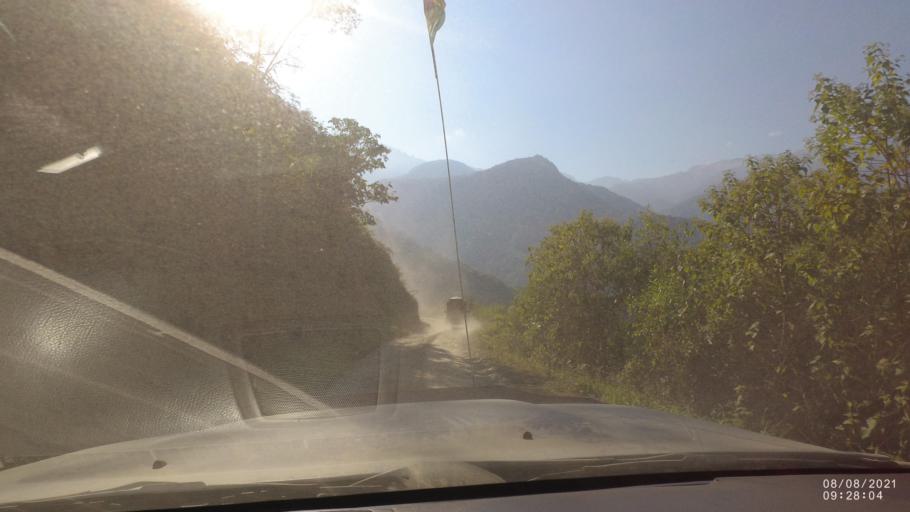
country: BO
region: La Paz
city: Quime
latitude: -16.5885
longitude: -66.7160
